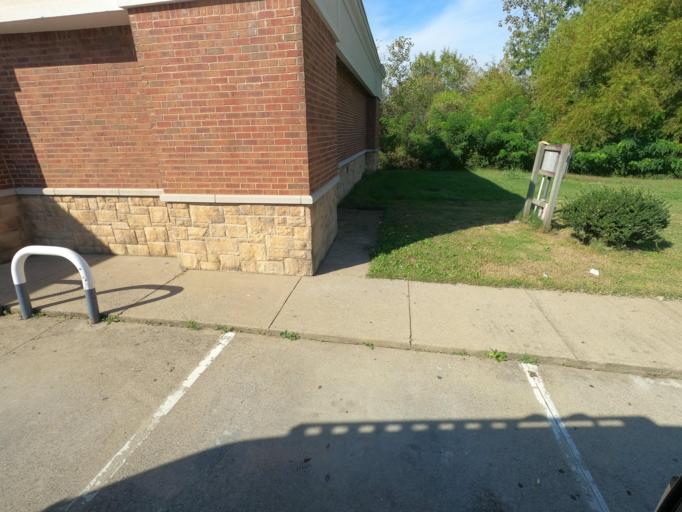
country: US
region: Tennessee
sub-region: Wilson County
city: Mount Juliet
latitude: 36.1728
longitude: -86.5138
